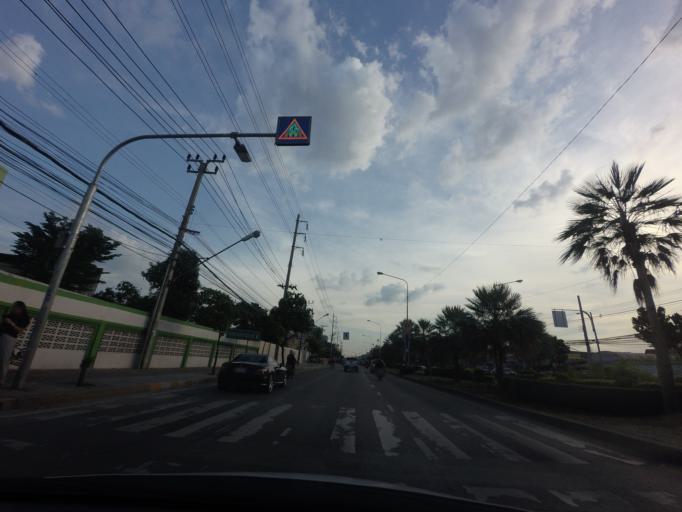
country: TH
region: Bangkok
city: Bang Khun Thian
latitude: 13.6441
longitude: 100.4319
